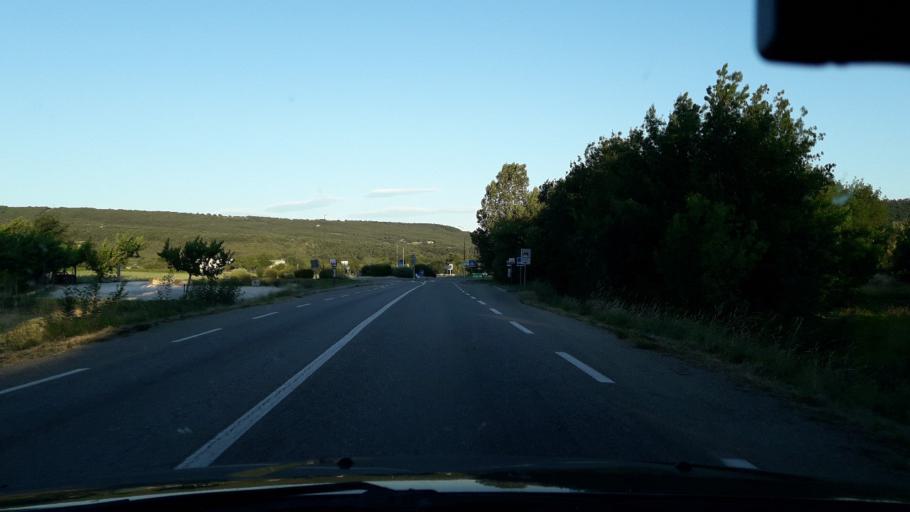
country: FR
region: Rhone-Alpes
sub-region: Departement de l'Ardeche
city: Alba-la-Romaine
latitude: 44.5632
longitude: 4.5946
